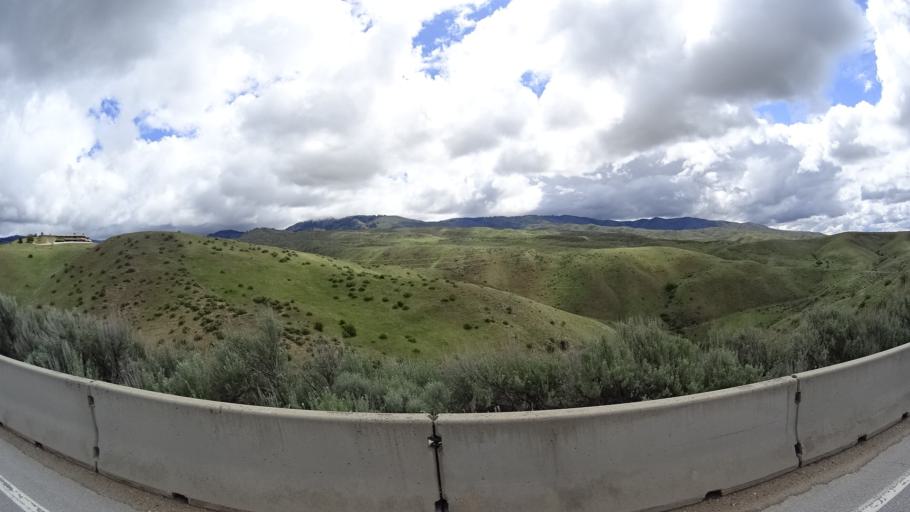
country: US
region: Idaho
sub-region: Ada County
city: Boise
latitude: 43.6935
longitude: -116.1706
